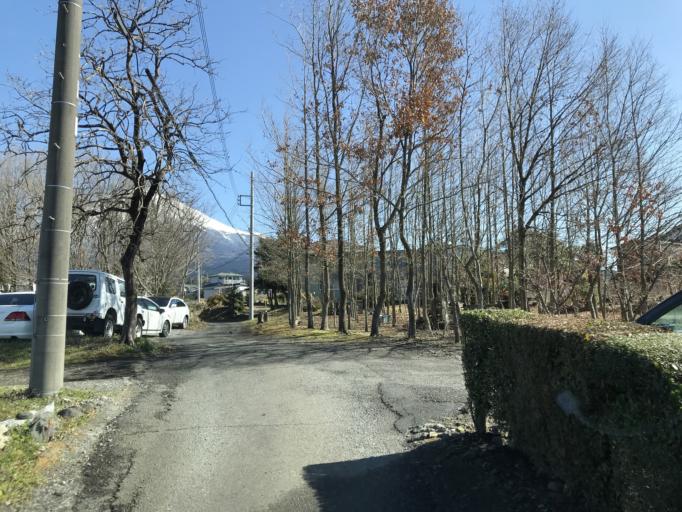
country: JP
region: Shizuoka
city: Fujinomiya
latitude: 35.2607
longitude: 138.6313
